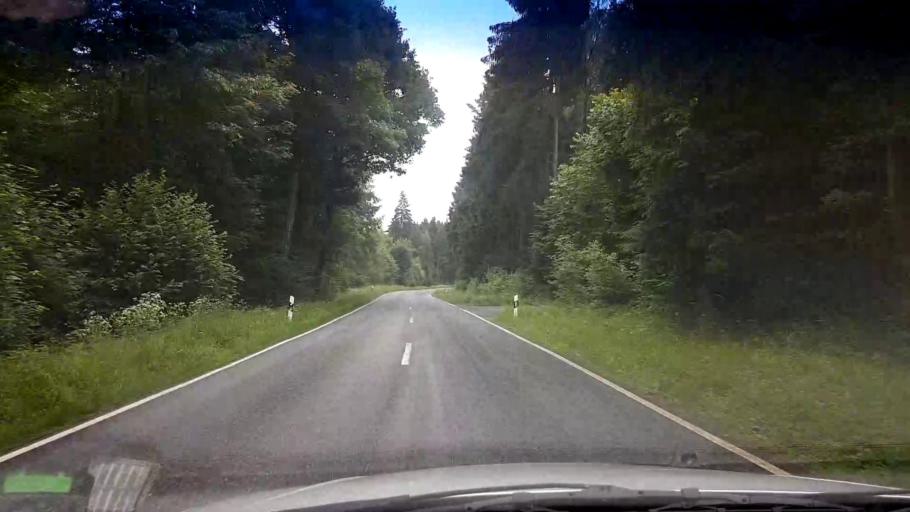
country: DE
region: Bavaria
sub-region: Upper Franconia
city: Weismain
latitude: 50.0841
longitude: 11.2951
